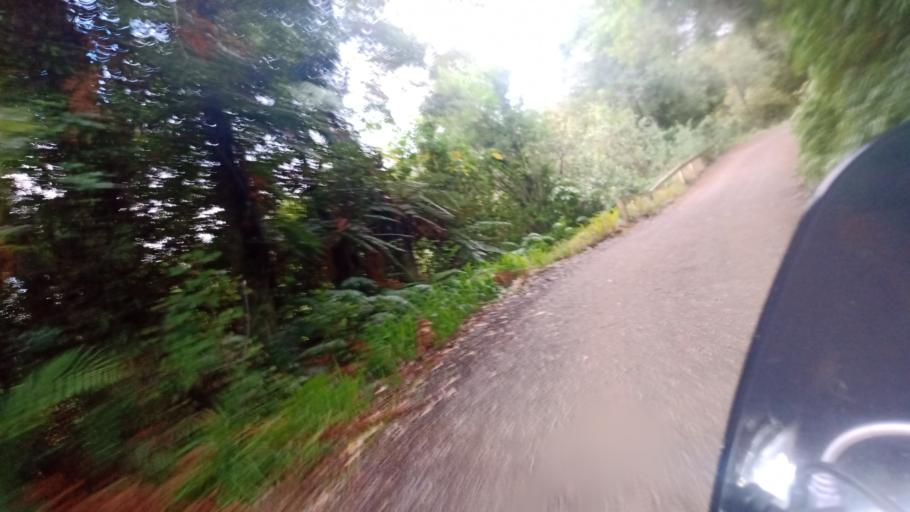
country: NZ
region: Hawke's Bay
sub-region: Wairoa District
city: Wairoa
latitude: -38.7310
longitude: 177.0890
